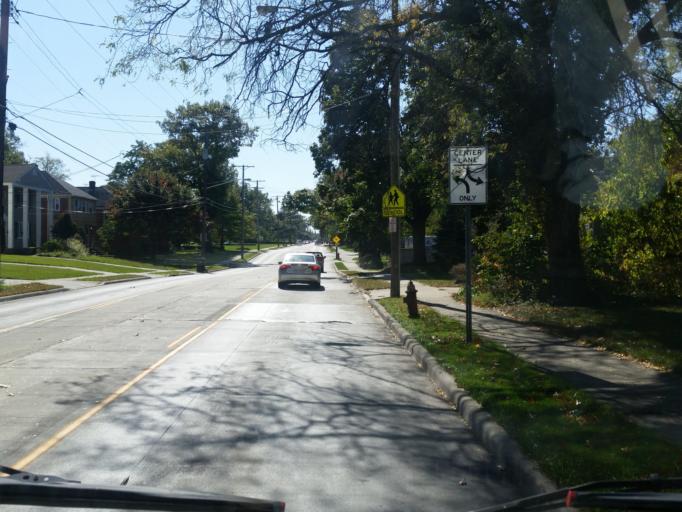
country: US
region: Ohio
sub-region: Cuyahoga County
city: Lakewood
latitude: 41.4621
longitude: -81.8140
